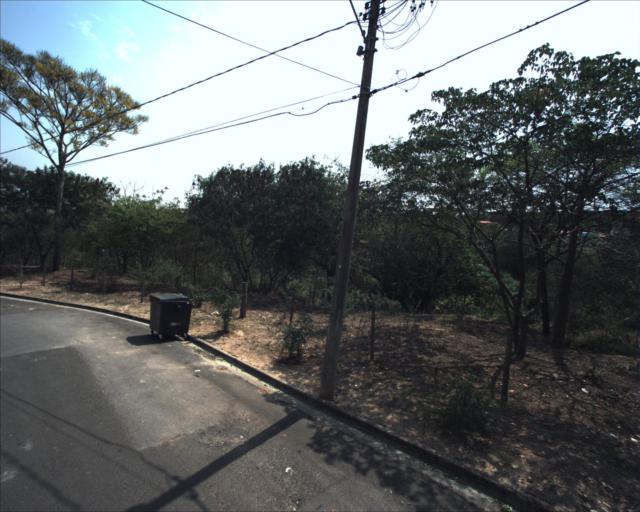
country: BR
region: Sao Paulo
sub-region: Sorocaba
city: Sorocaba
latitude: -23.4409
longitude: -47.4812
